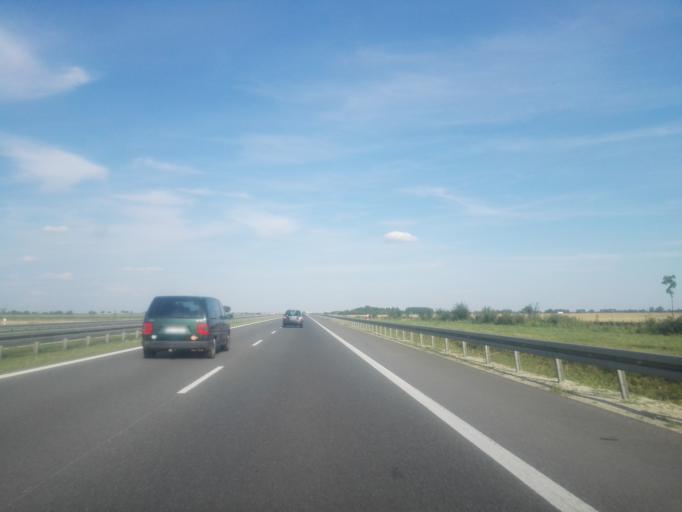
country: PL
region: Lower Silesian Voivodeship
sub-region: Powiat olesnicki
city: Dobroszyce
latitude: 51.2237
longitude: 17.2979
